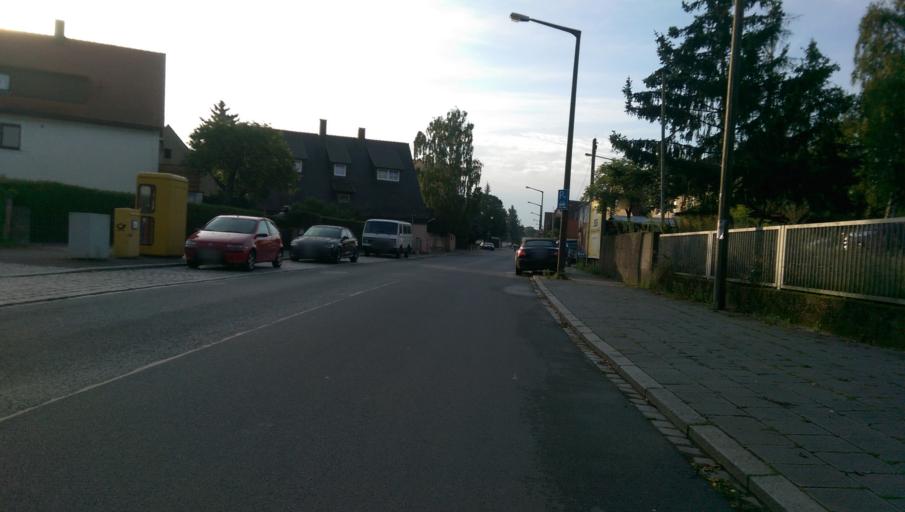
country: DE
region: Bavaria
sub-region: Regierungsbezirk Mittelfranken
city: Wetzendorf
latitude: 49.4708
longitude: 11.0393
